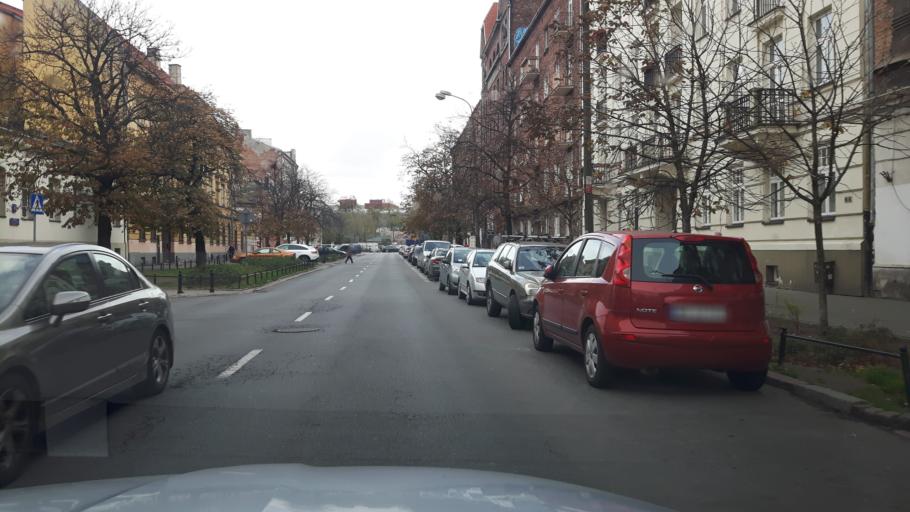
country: PL
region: Masovian Voivodeship
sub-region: Warszawa
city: Praga Polnoc
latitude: 52.2578
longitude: 21.0355
